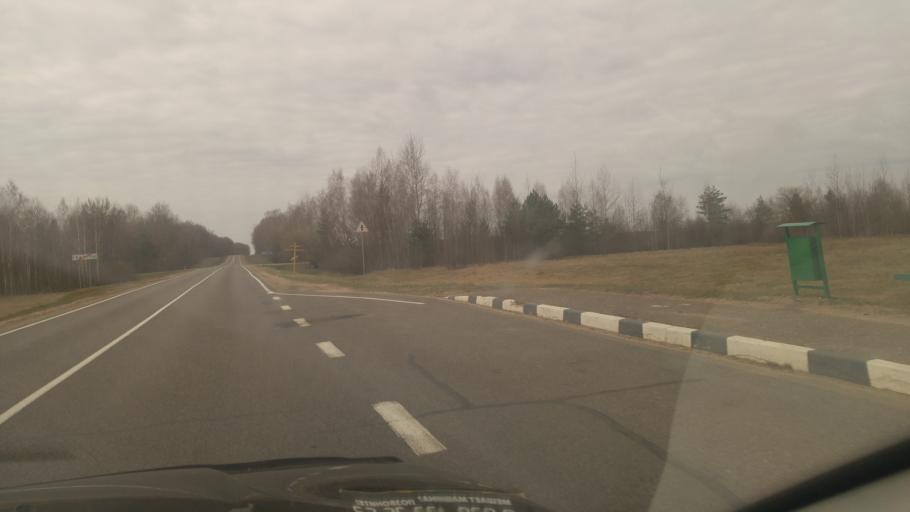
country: BY
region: Minsk
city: Chervyen'
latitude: 53.6619
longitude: 28.3290
